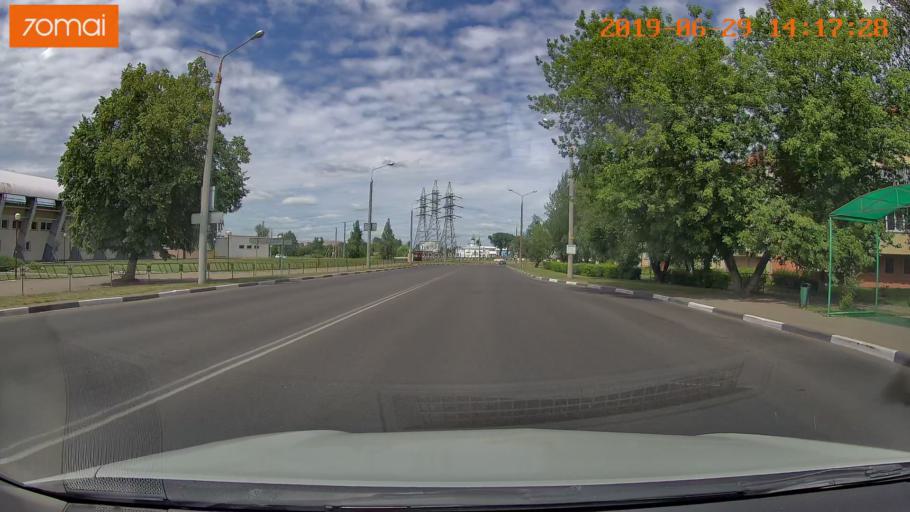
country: BY
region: Minsk
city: Salihorsk
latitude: 52.7986
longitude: 27.5397
